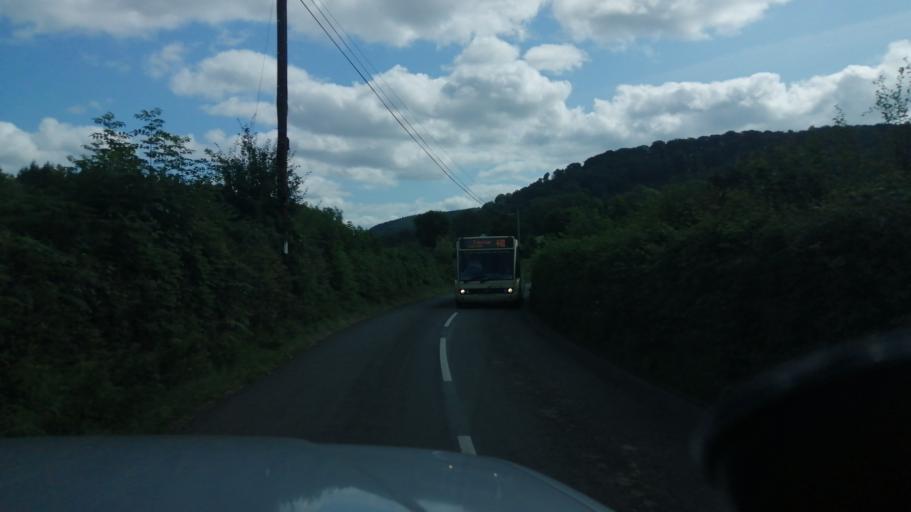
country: GB
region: England
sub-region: Herefordshire
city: Moccas
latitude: 52.0881
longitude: -2.9727
